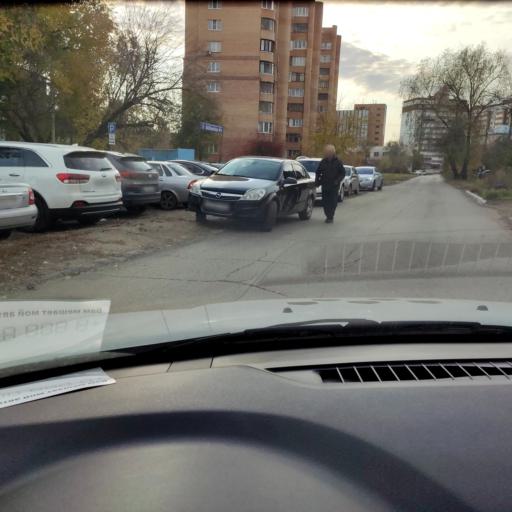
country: RU
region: Samara
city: Tol'yatti
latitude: 53.5247
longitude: 49.4189
